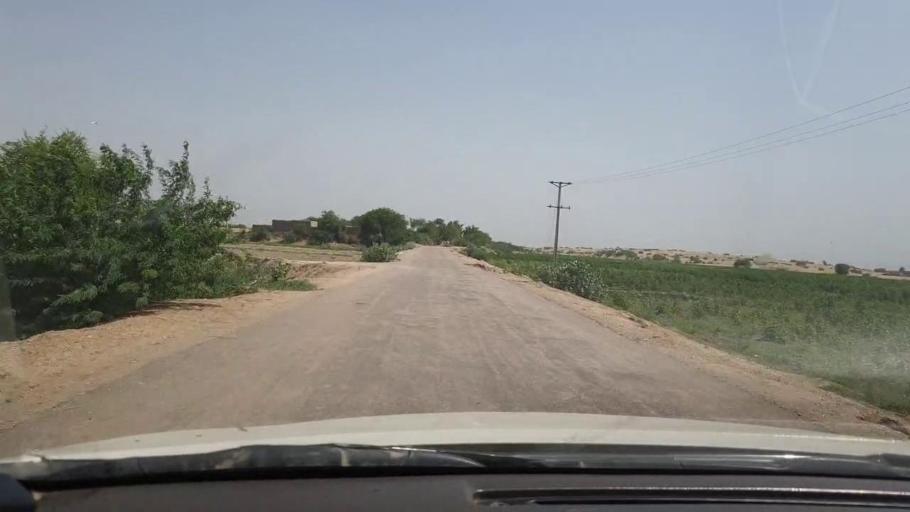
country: PK
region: Sindh
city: Rohri
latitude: 27.5018
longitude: 69.0418
